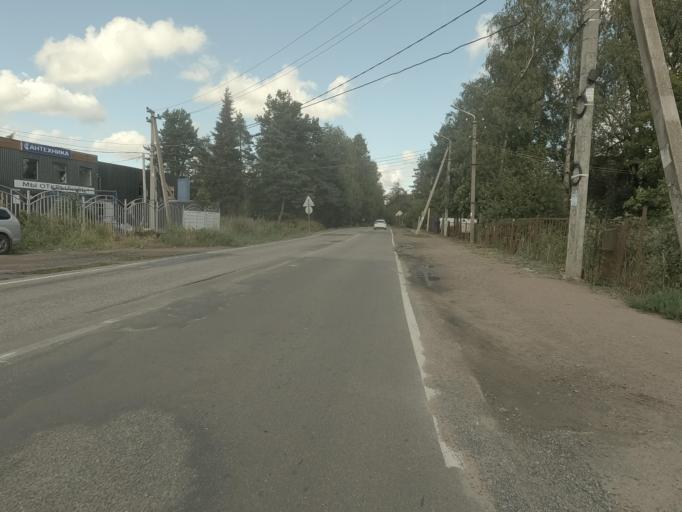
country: RU
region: Leningrad
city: Vsevolozhsk
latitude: 60.0191
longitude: 30.6838
